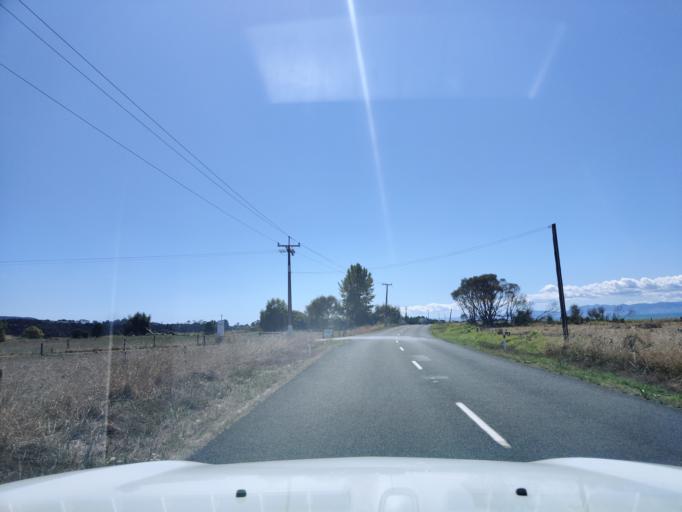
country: NZ
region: Waikato
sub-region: Thames-Coromandel District
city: Thames
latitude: -37.0686
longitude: 175.2959
